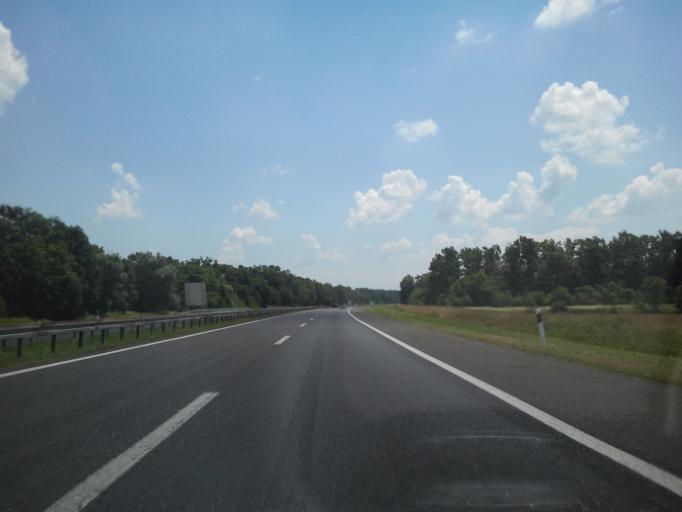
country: HR
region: Zagrebacka
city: Lupoglav
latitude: 45.7485
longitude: 16.3108
